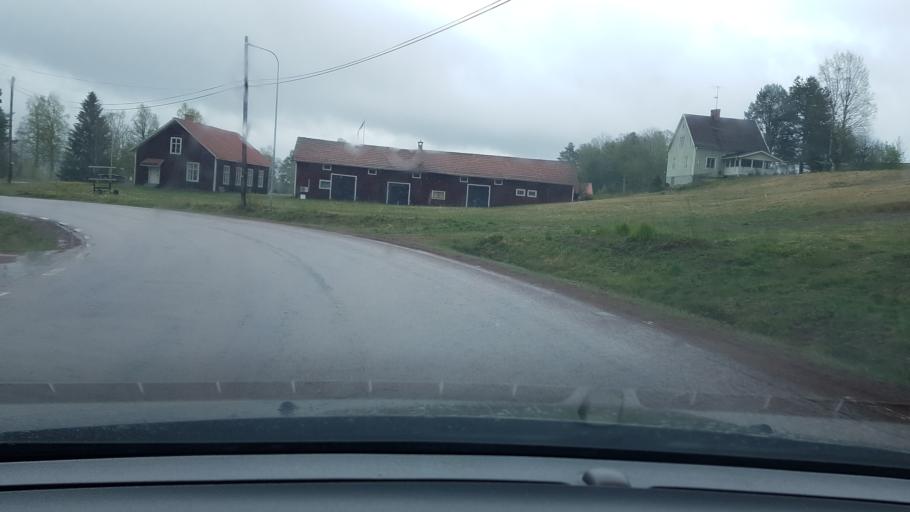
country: SE
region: Dalarna
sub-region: Alvdalens Kommun
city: AElvdalen
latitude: 61.1162
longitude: 14.1724
